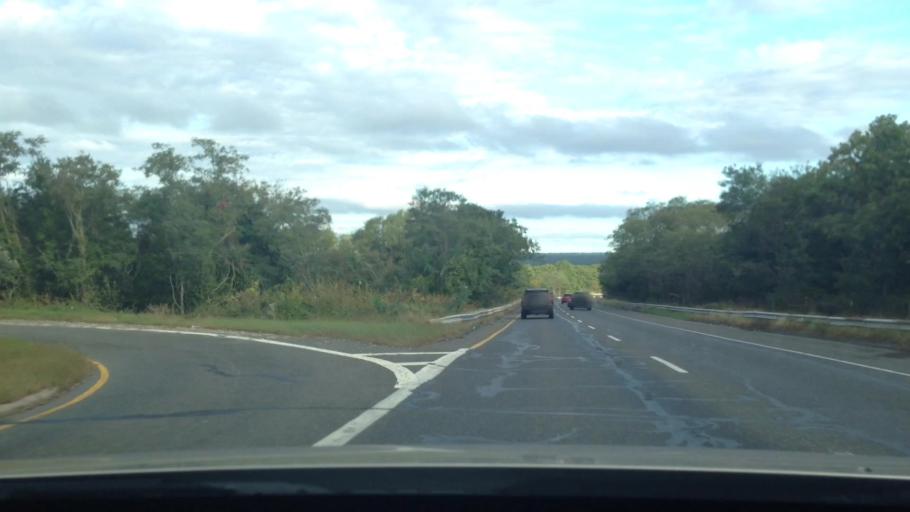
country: US
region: New York
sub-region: Suffolk County
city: Selden
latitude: 40.8523
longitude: -73.0189
